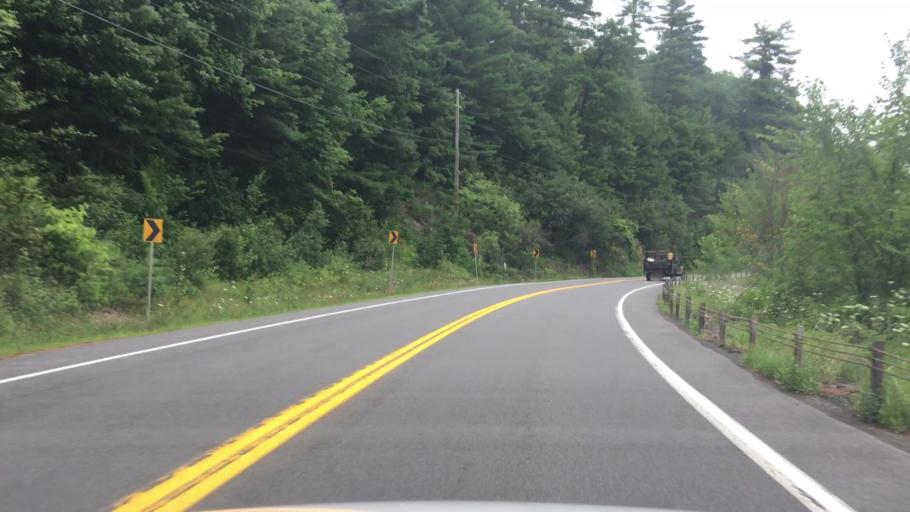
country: US
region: New York
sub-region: Clinton County
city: Peru
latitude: 44.4492
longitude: -73.6549
